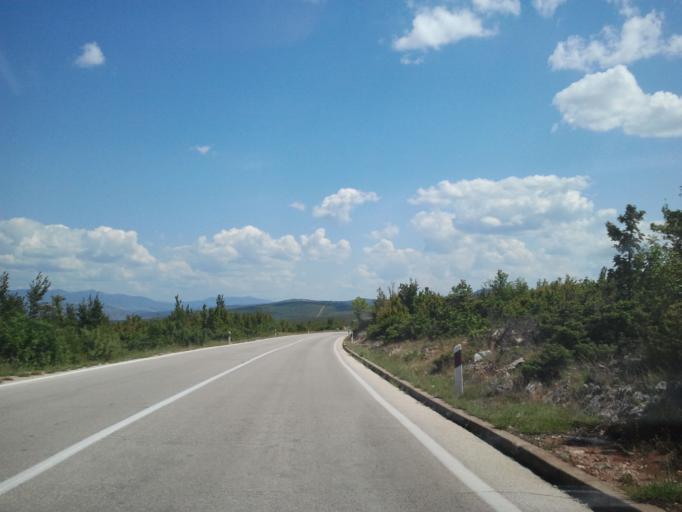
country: HR
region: Zadarska
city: Obrovac
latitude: 44.1970
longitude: 15.6660
